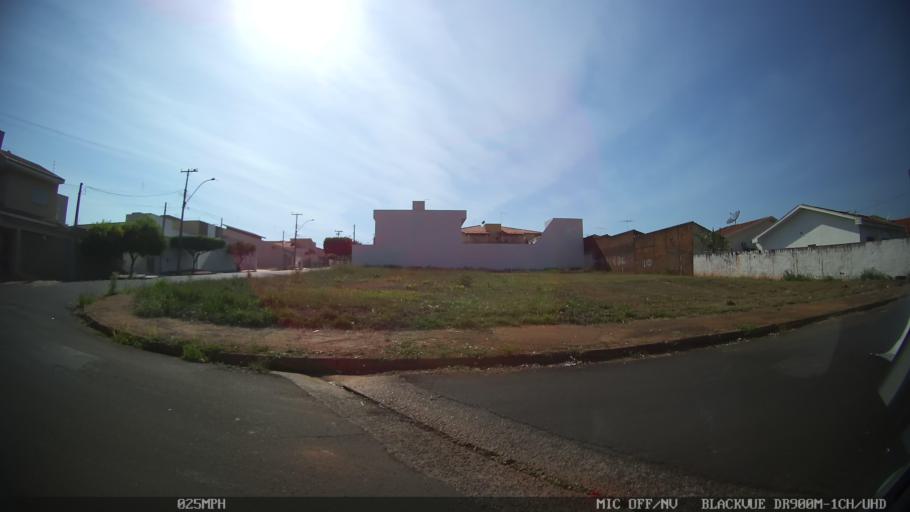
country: BR
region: Sao Paulo
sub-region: Sao Jose Do Rio Preto
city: Sao Jose do Rio Preto
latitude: -20.8016
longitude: -49.4130
